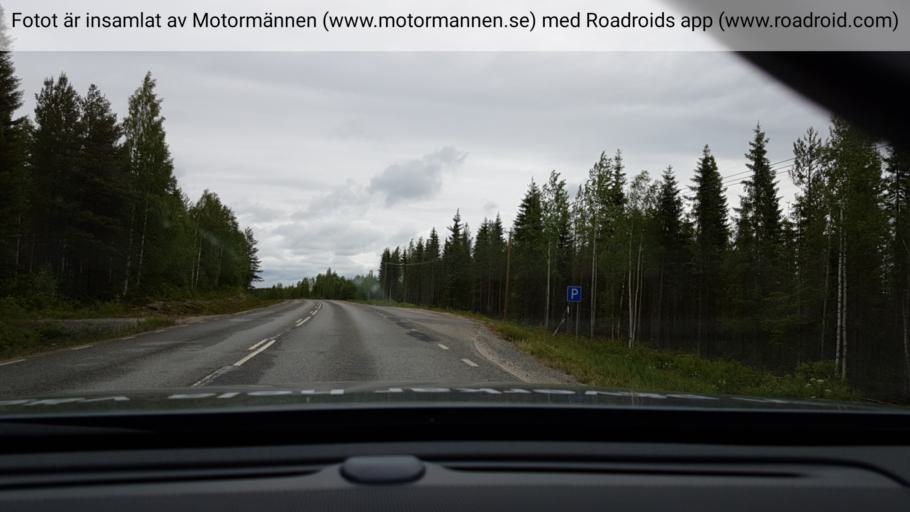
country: SE
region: Vaesterbotten
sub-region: Lycksele Kommun
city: Lycksele
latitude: 64.5394
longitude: 18.4980
